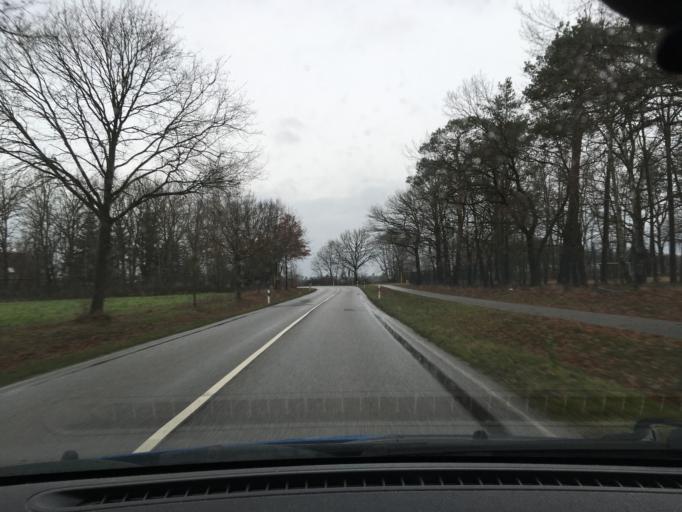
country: DE
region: Schleswig-Holstein
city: Lanze
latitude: 53.3764
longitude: 10.6304
